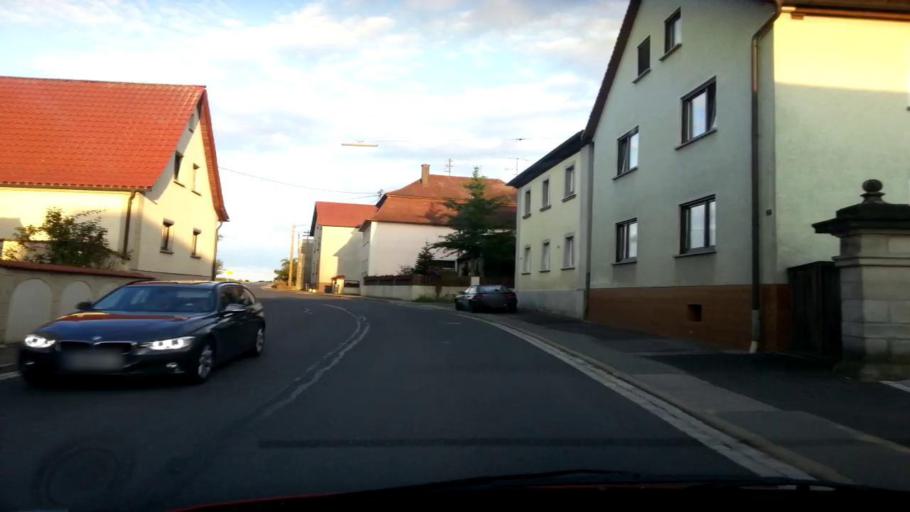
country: DE
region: Bavaria
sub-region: Upper Franconia
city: Burgwindheim
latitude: 49.8232
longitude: 10.6362
